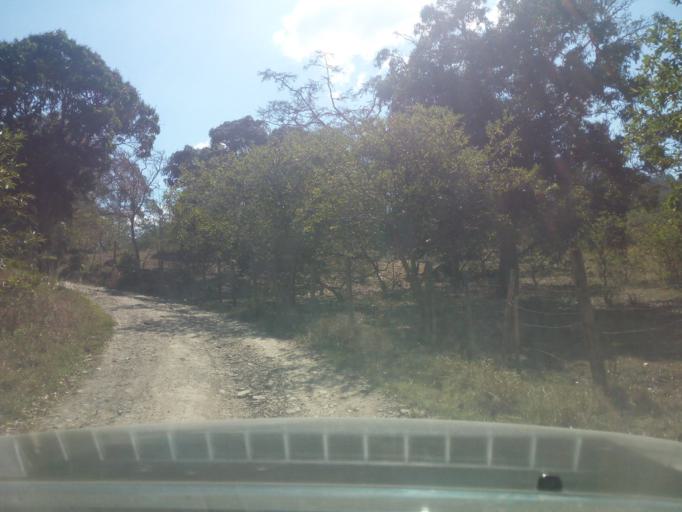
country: CO
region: Boyaca
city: Guateque
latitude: 4.9891
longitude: -73.4627
